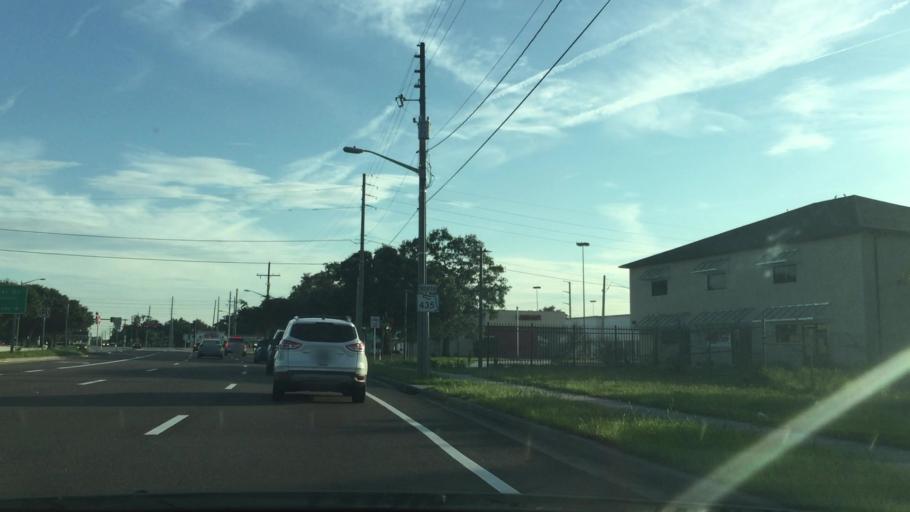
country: US
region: Florida
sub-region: Orange County
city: Pine Hills
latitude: 28.5499
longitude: -81.4567
